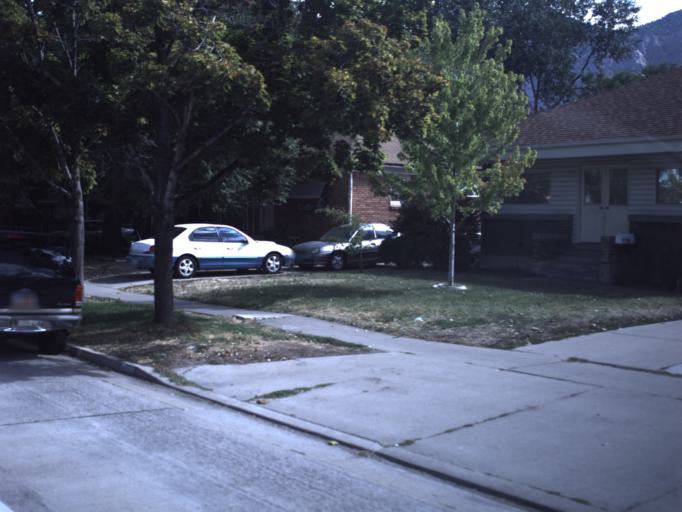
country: US
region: Utah
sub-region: Weber County
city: Ogden
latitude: 41.2505
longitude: -111.9697
